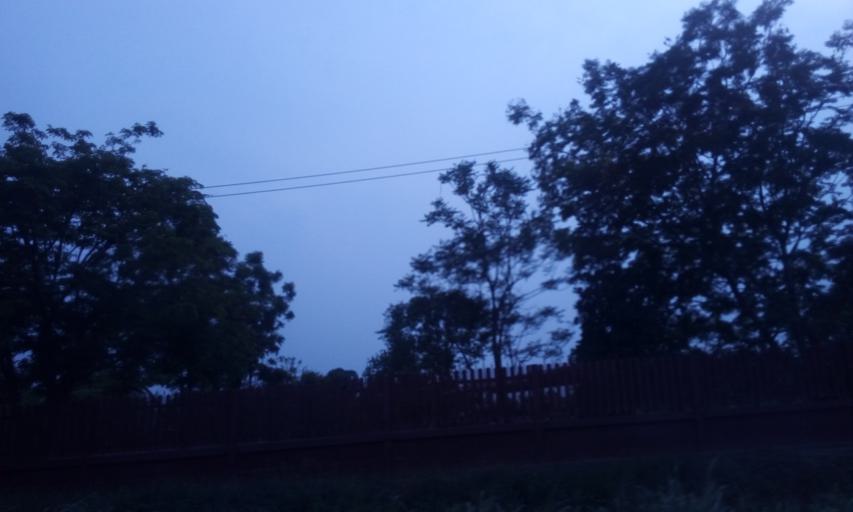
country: TH
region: Chachoengsao
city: Plaeng Yao
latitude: 13.5743
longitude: 101.2576
